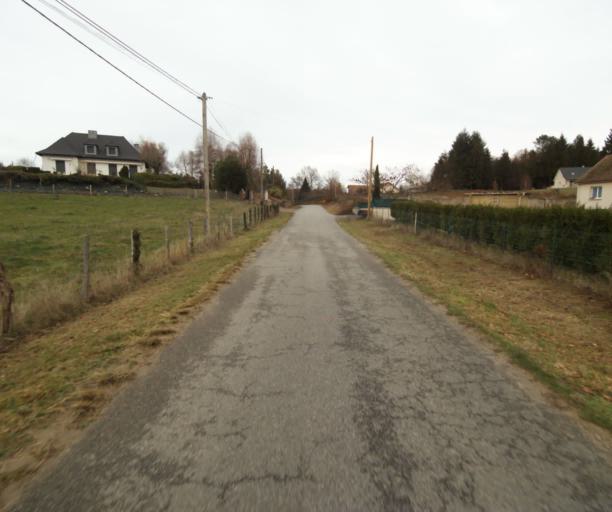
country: FR
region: Limousin
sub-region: Departement de la Correze
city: Saint-Mexant
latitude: 45.2614
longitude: 1.6639
